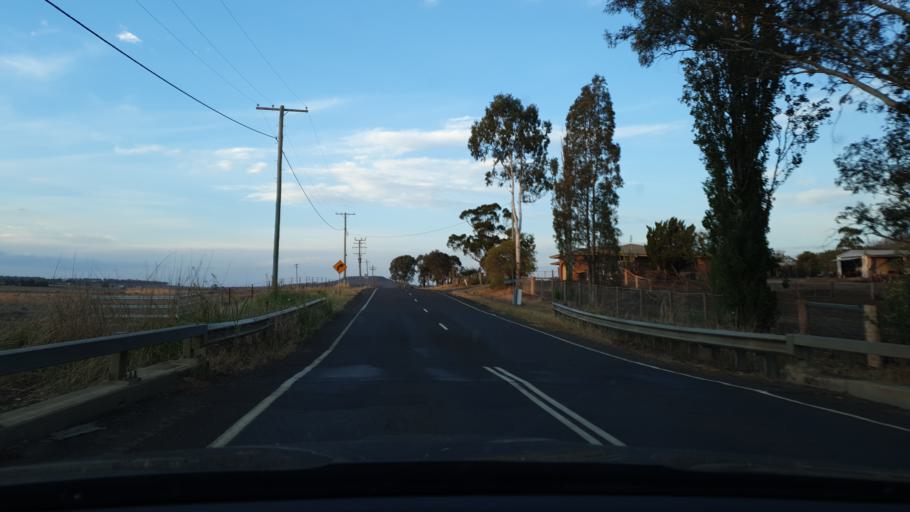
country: AU
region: Queensland
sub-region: Southern Downs
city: Warwick
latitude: -28.0280
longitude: 151.9829
